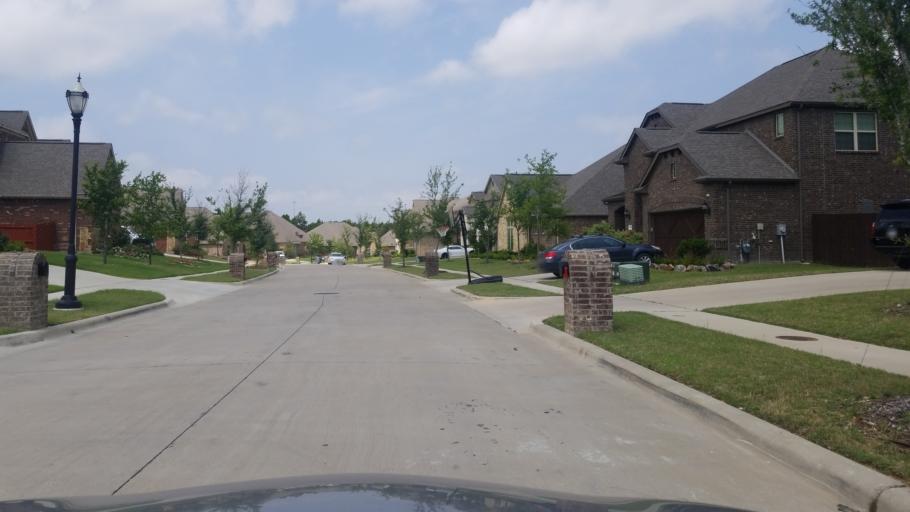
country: US
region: Texas
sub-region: Dallas County
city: Duncanville
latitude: 32.6819
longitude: -96.9366
